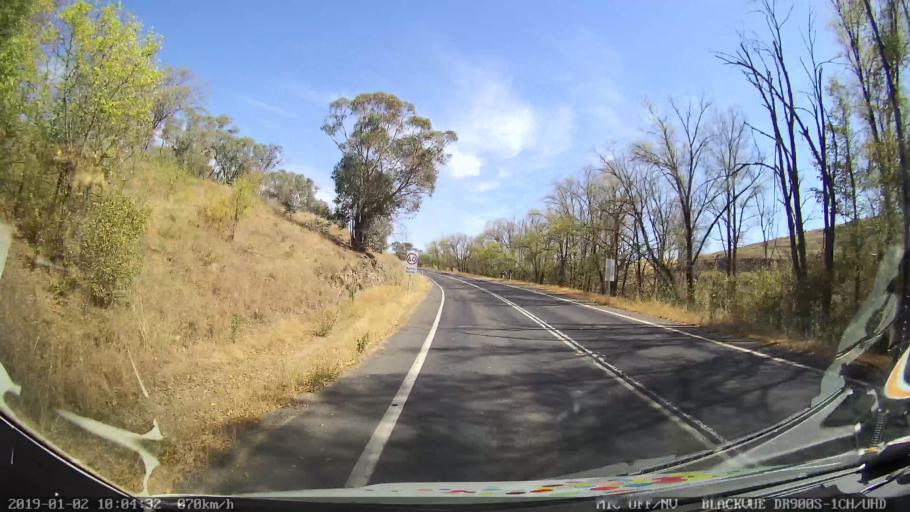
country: AU
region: New South Wales
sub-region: Gundagai
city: Gundagai
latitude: -35.1666
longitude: 148.1230
